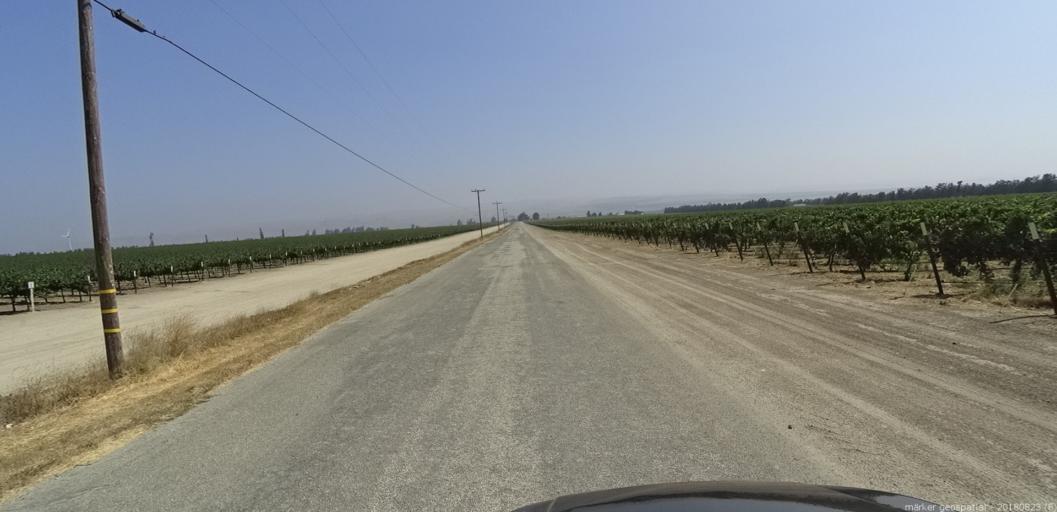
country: US
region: California
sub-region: Monterey County
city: King City
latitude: 36.2521
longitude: -121.1972
